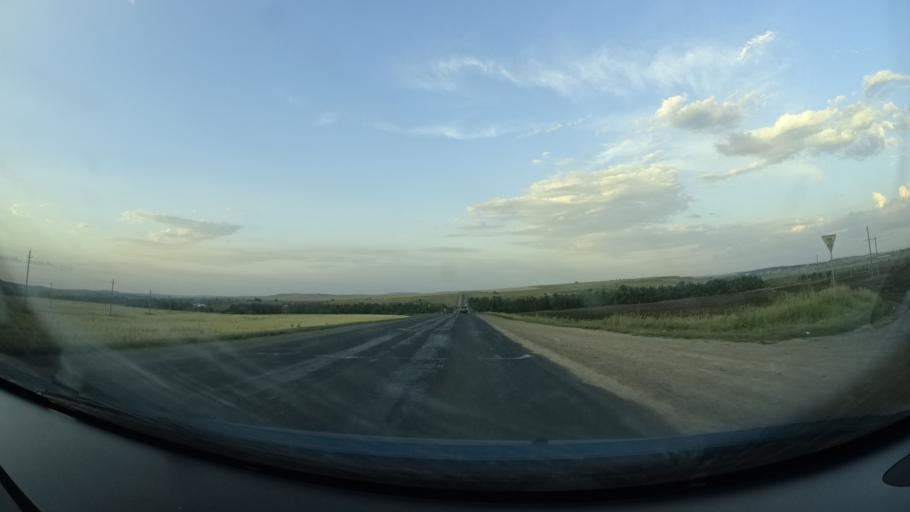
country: RU
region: Orenburg
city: Severnoye
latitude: 54.1012
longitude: 52.4844
